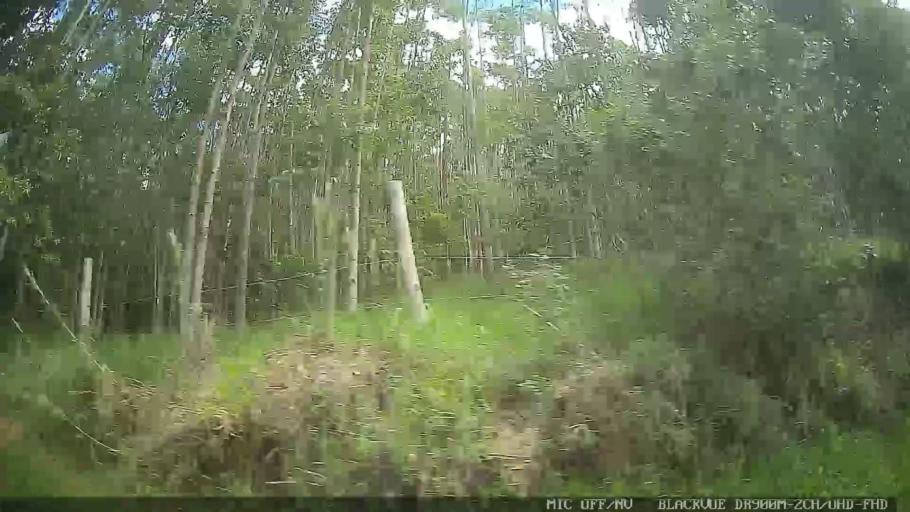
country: BR
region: Sao Paulo
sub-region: Caraguatatuba
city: Caraguatatuba
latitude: -23.5501
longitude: -45.6045
